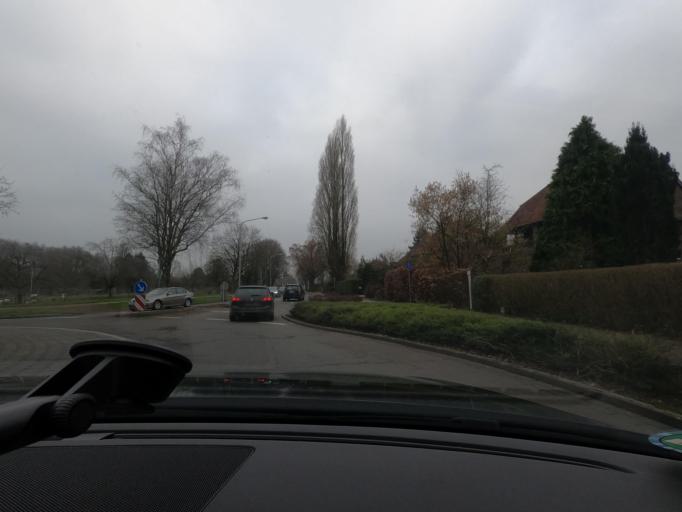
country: DE
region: North Rhine-Westphalia
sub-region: Regierungsbezirk Dusseldorf
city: Krefeld
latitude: 51.3632
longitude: 6.5695
